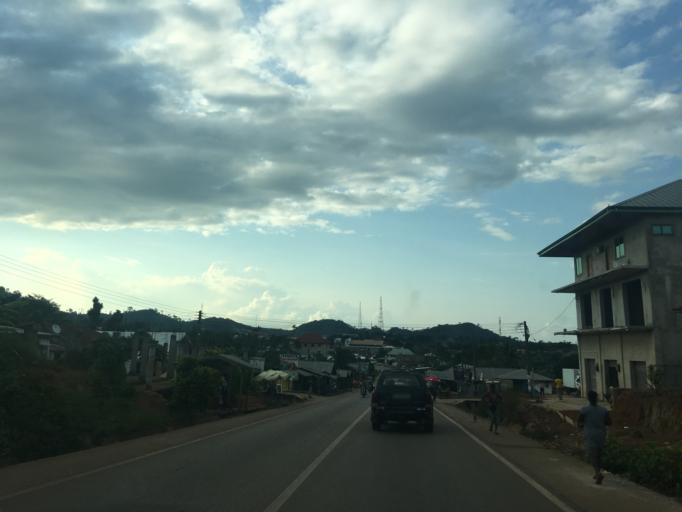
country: GH
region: Western
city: Bibiani
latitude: 6.4463
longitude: -2.3146
